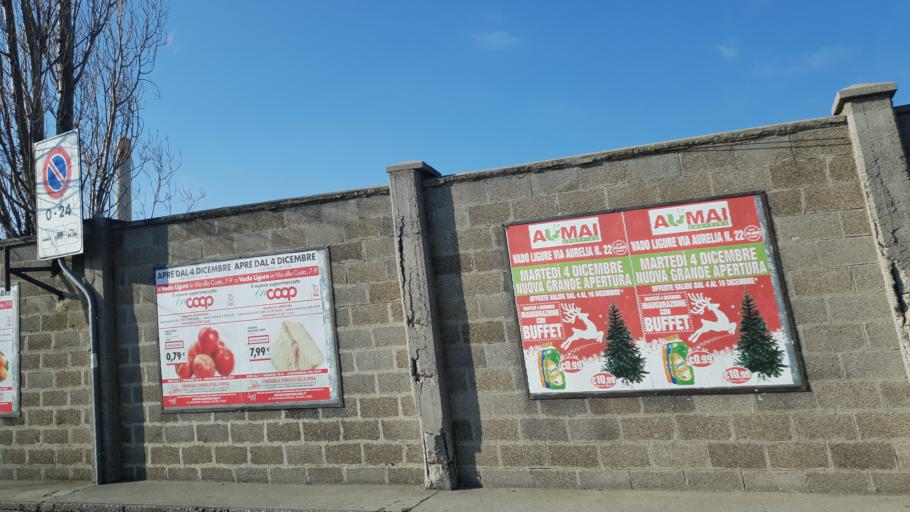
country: IT
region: Liguria
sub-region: Provincia di Savona
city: Valleggia
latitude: 44.2802
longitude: 8.4429
